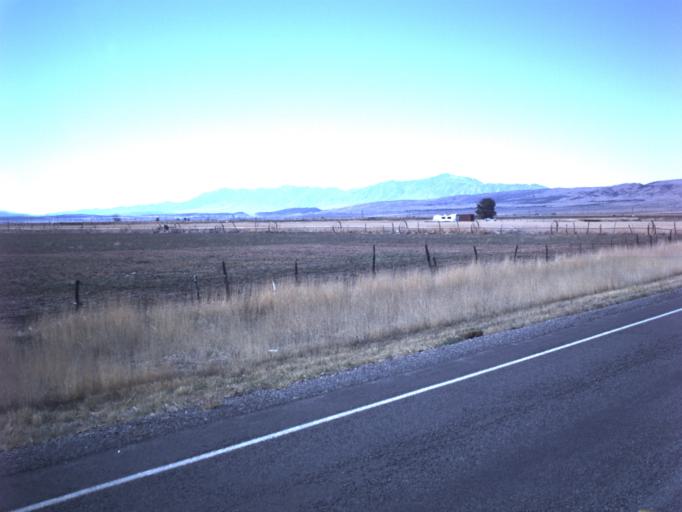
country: US
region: Utah
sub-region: Juab County
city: Nephi
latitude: 39.5583
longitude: -111.8810
